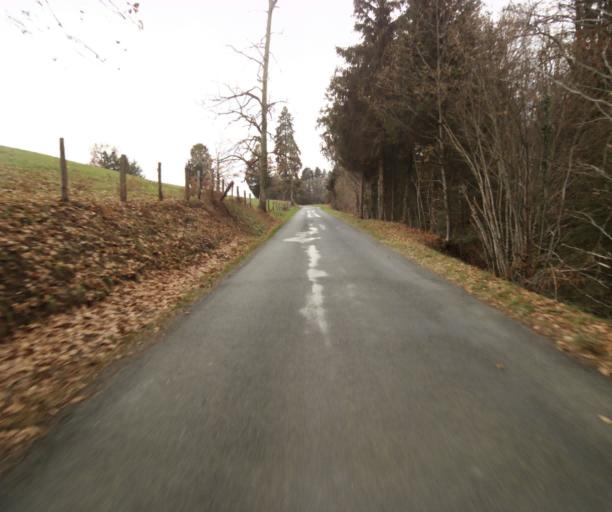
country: FR
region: Limousin
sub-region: Departement de la Correze
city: Chameyrat
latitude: 45.2600
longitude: 1.6790
